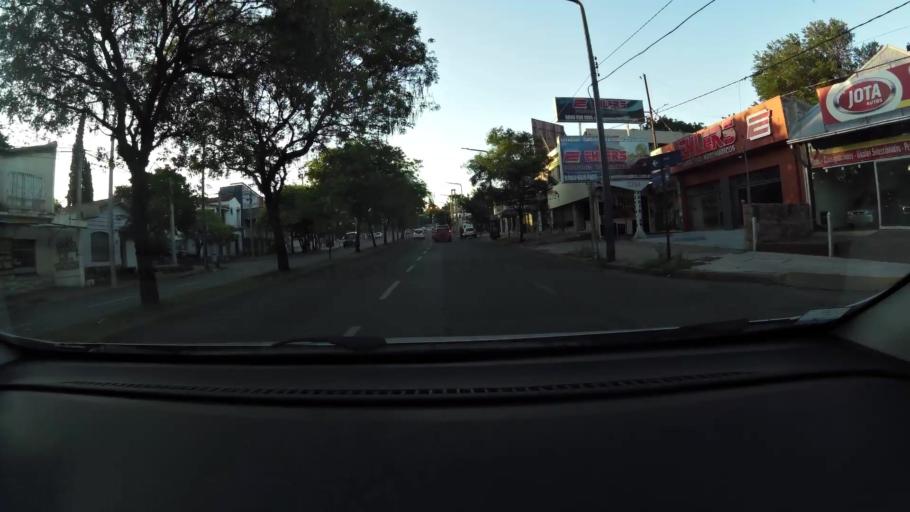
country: AR
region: Cordoba
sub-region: Departamento de Capital
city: Cordoba
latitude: -31.3838
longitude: -64.2216
